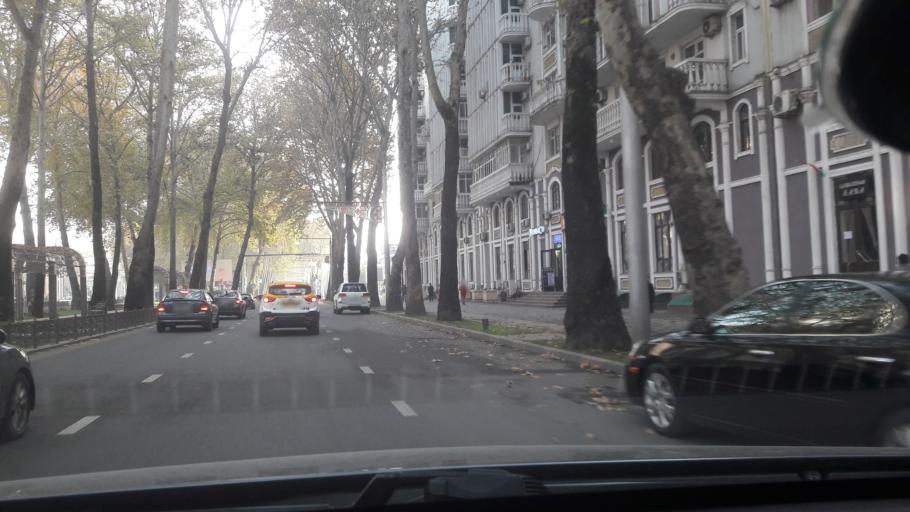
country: TJ
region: Dushanbe
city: Dushanbe
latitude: 38.5724
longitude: 68.7880
